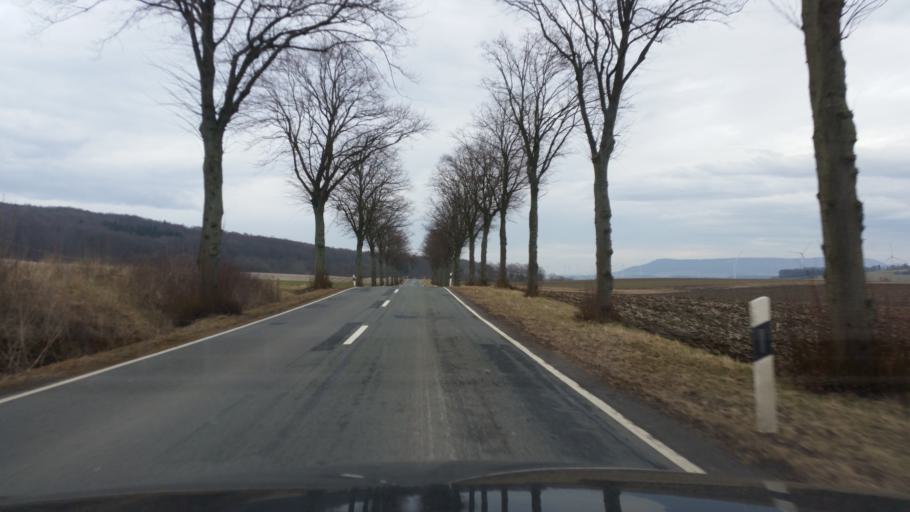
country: DE
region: Lower Saxony
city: Hameln
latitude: 52.1522
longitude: 9.3845
